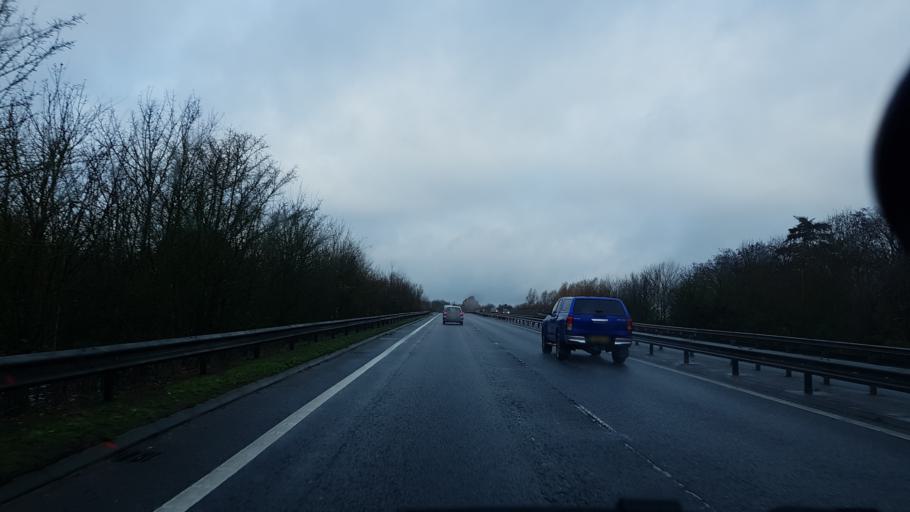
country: GB
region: England
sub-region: Bracknell Forest
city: Binfield
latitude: 51.4117
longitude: -0.7970
